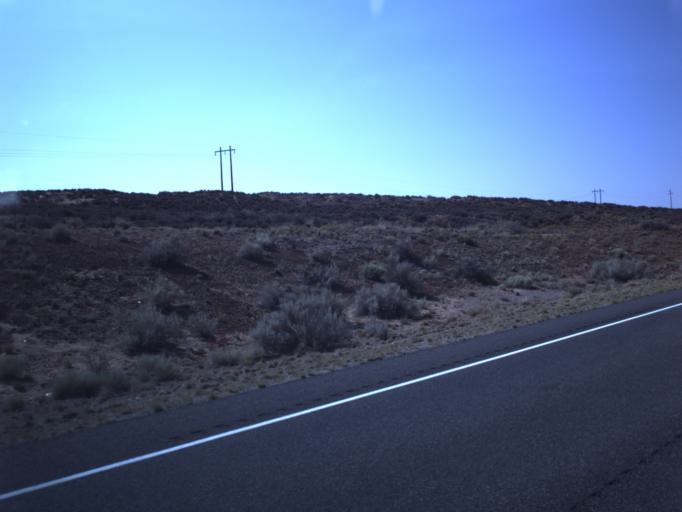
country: US
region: Utah
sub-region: San Juan County
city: Blanding
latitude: 37.3584
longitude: -109.5152
